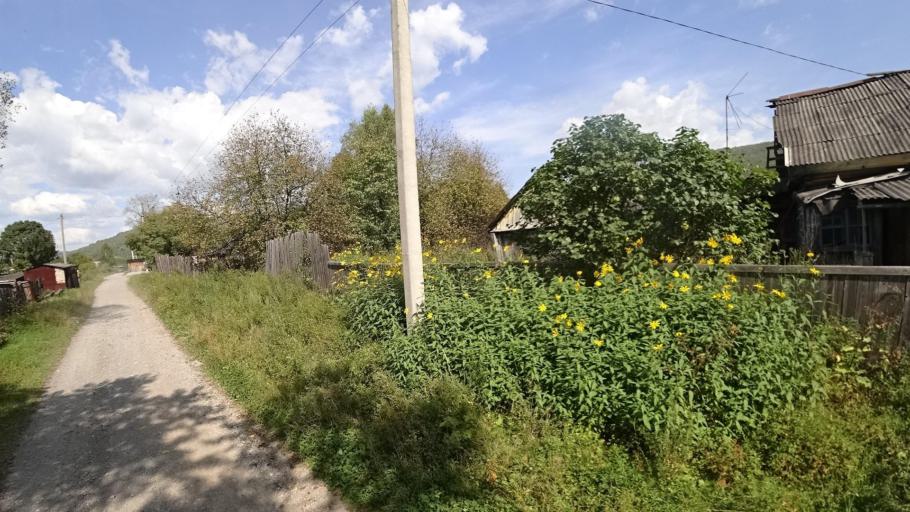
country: RU
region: Jewish Autonomous Oblast
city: Londoko
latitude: 49.0234
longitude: 131.9331
